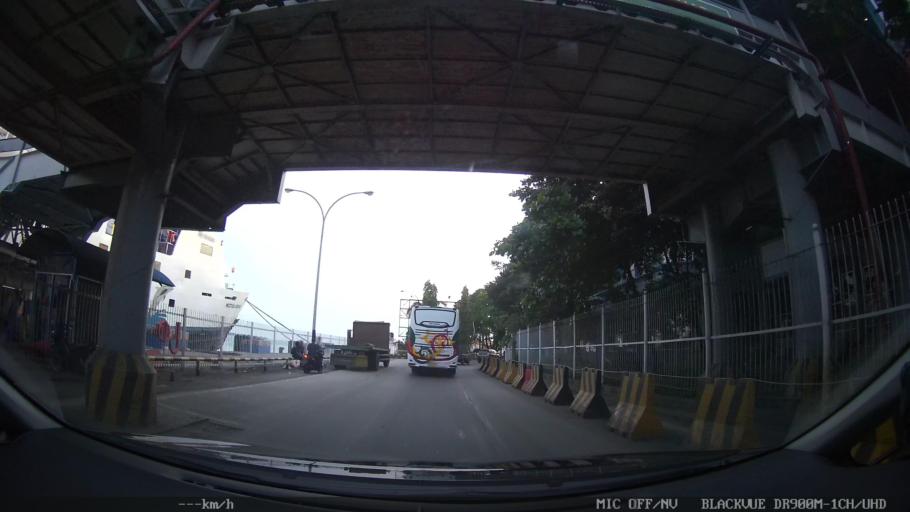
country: ID
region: Lampung
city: Penengahan
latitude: -5.8692
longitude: 105.7554
